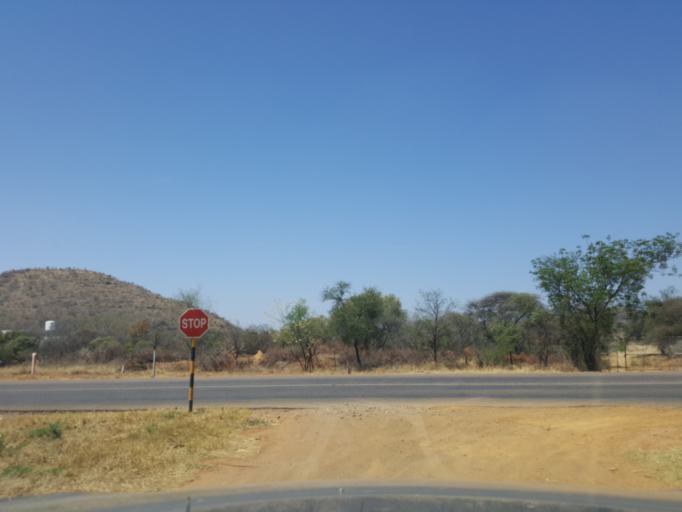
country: BW
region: South East
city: Lobatse
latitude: -25.1589
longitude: 25.6891
